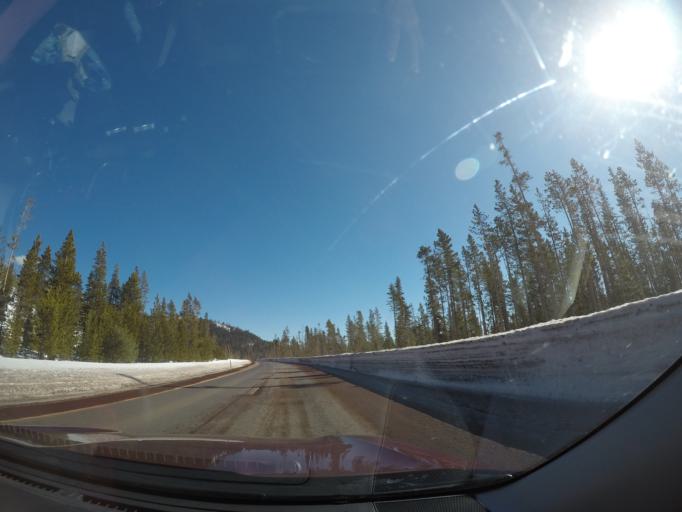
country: US
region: Oregon
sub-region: Deschutes County
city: Sunriver
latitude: 43.9822
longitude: -121.6128
